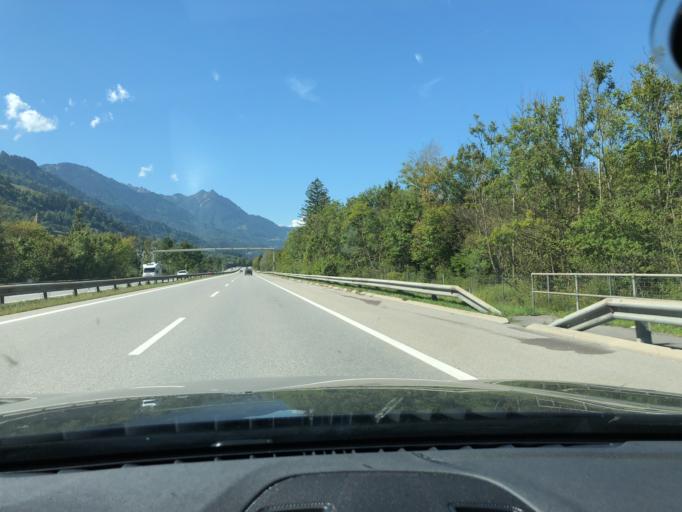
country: AT
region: Vorarlberg
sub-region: Politischer Bezirk Bludenz
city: Thuringen
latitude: 47.1754
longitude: 9.7519
